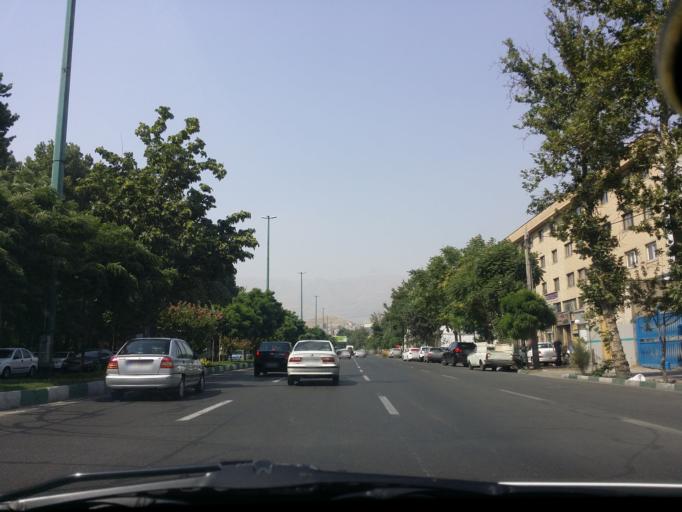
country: IR
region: Alborz
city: Karaj
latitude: 35.8039
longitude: 51.0016
